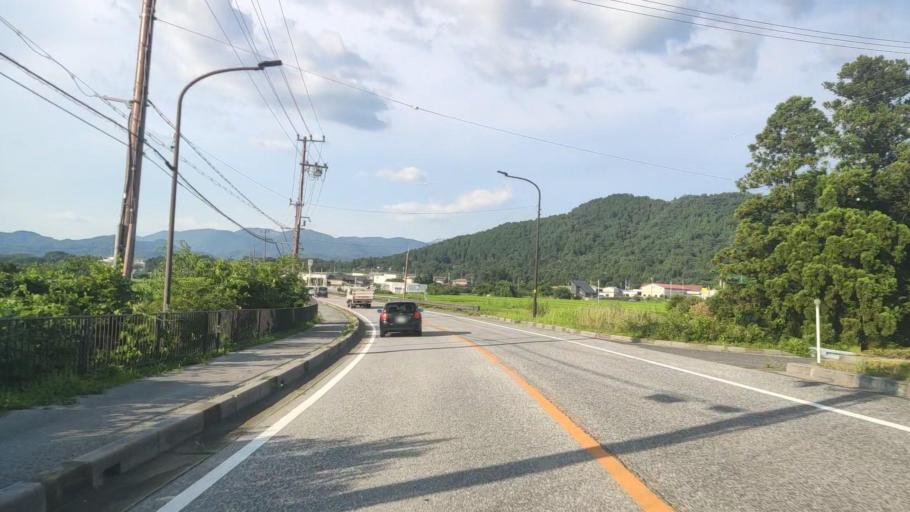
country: JP
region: Shiga Prefecture
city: Hikone
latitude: 35.2078
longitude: 136.2785
